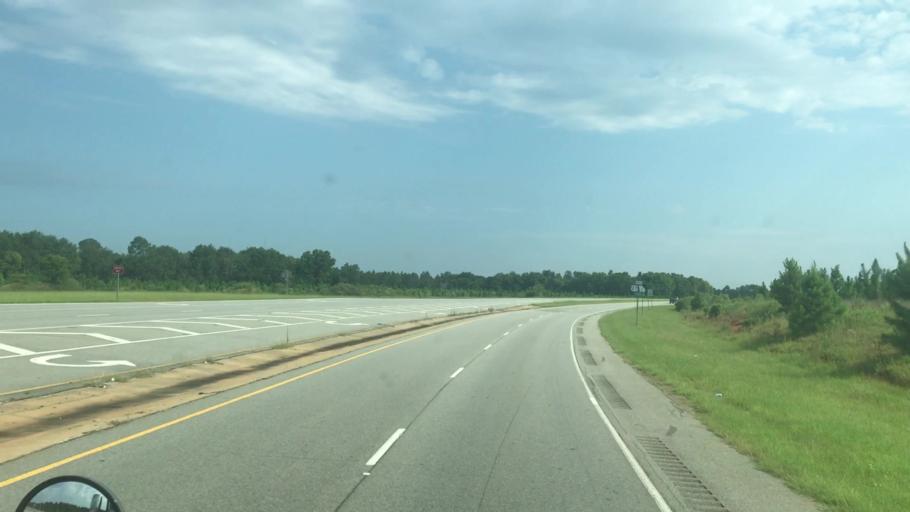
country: US
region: Georgia
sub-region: Early County
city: Blakely
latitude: 31.3583
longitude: -84.9232
